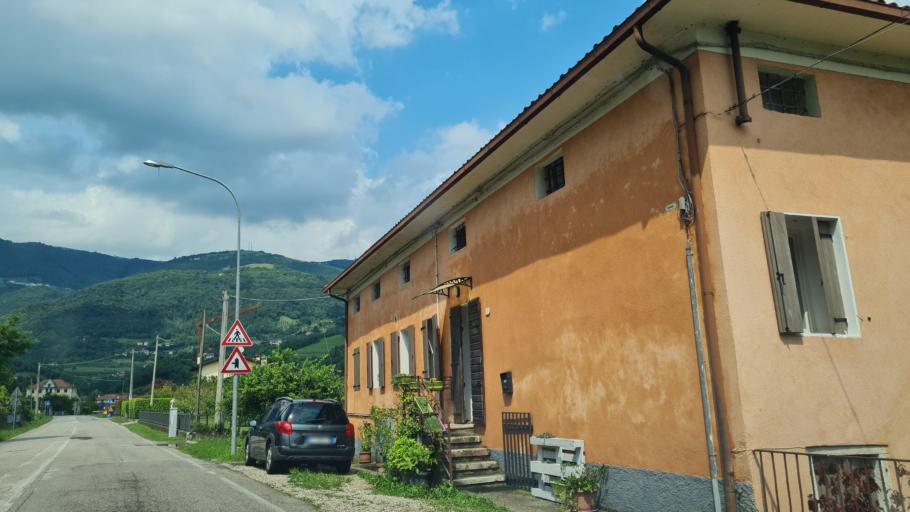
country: IT
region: Veneto
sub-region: Provincia di Vicenza
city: Marostica
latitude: 45.7620
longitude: 11.6610
